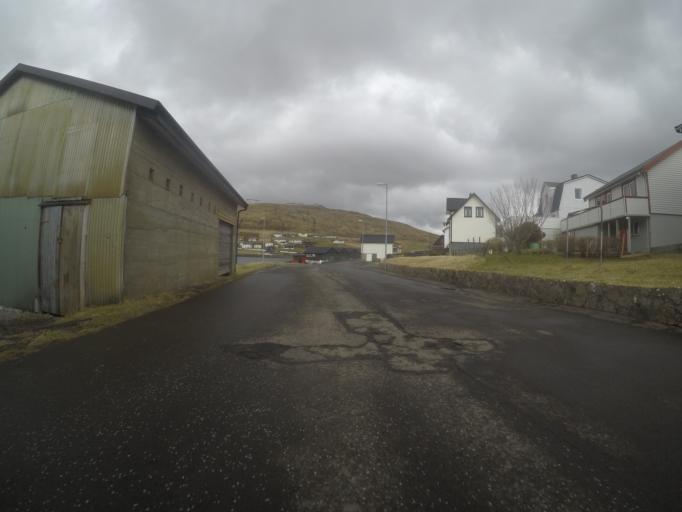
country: FO
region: Vagar
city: Midvagur
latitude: 62.0506
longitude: -7.1509
